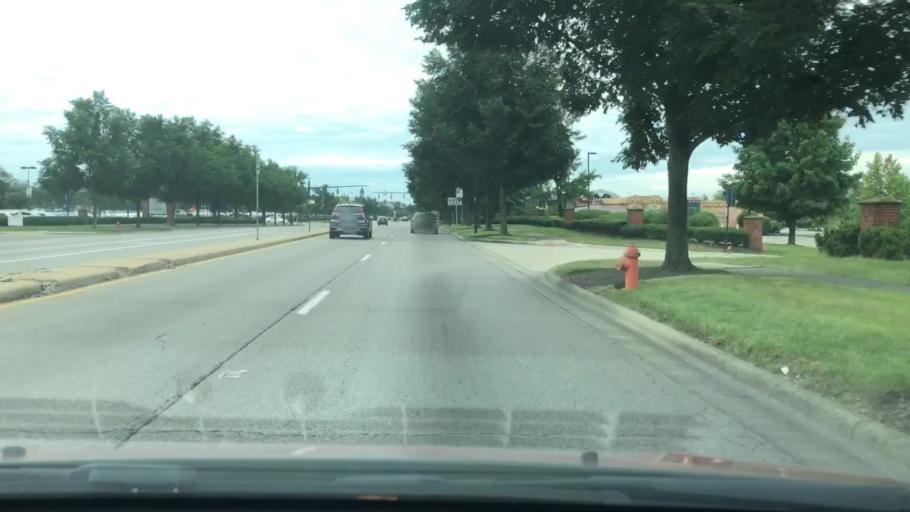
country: US
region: Ohio
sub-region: Franklin County
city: Huber Ridge
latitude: 40.0571
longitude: -82.9184
